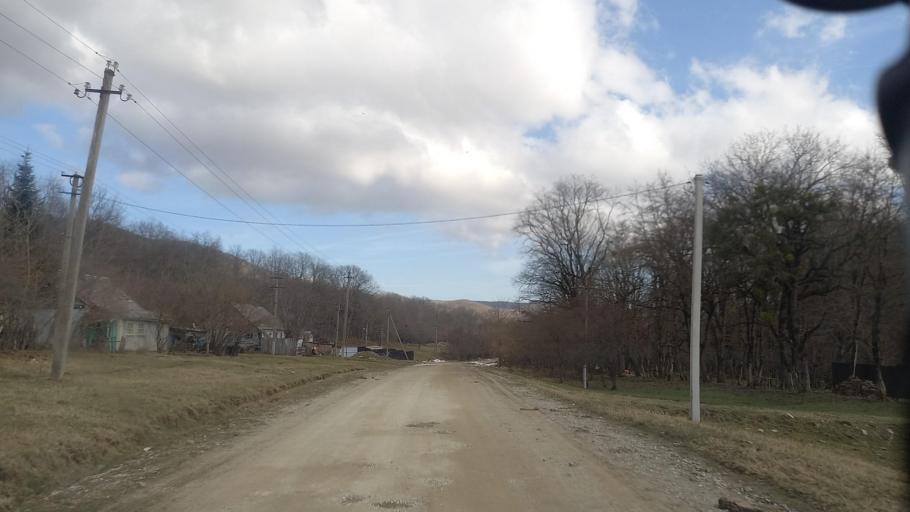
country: RU
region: Krasnodarskiy
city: Smolenskaya
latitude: 44.6028
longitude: 38.8628
